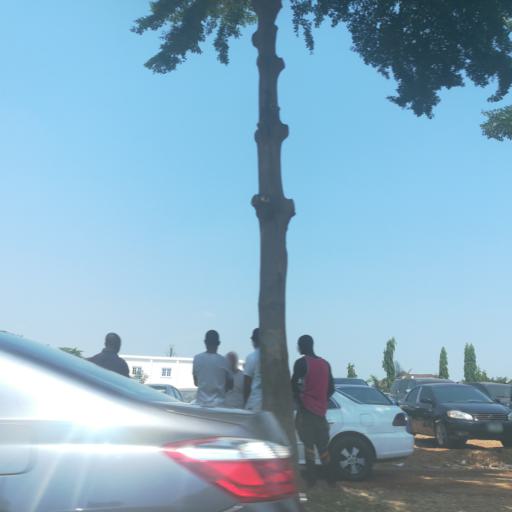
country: NG
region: Abuja Federal Capital Territory
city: Abuja
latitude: 9.0721
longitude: 7.4376
